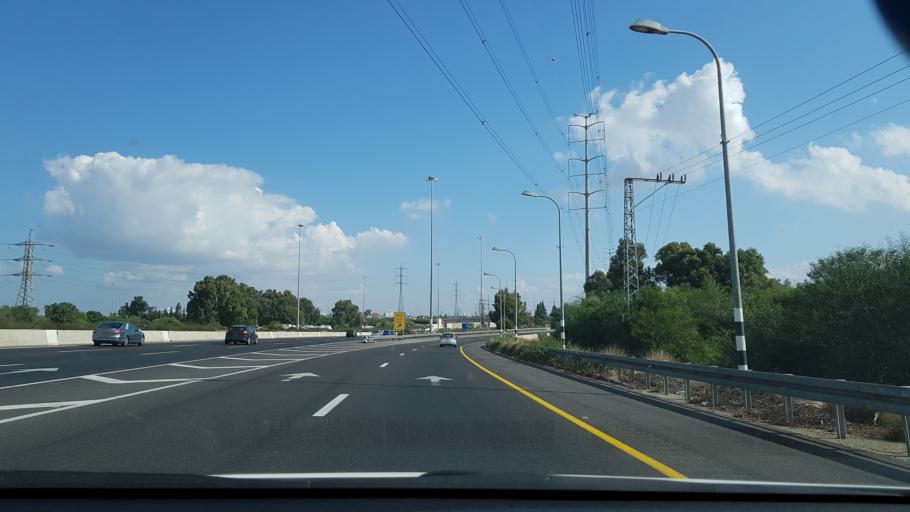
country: IL
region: Central District
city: Bet Dagan
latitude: 31.9961
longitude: 34.8007
